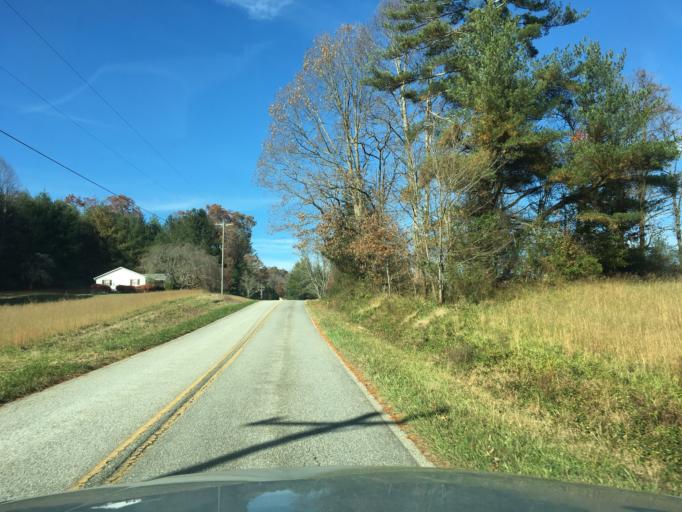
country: US
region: North Carolina
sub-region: Henderson County
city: Etowah
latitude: 35.3288
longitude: -82.6148
